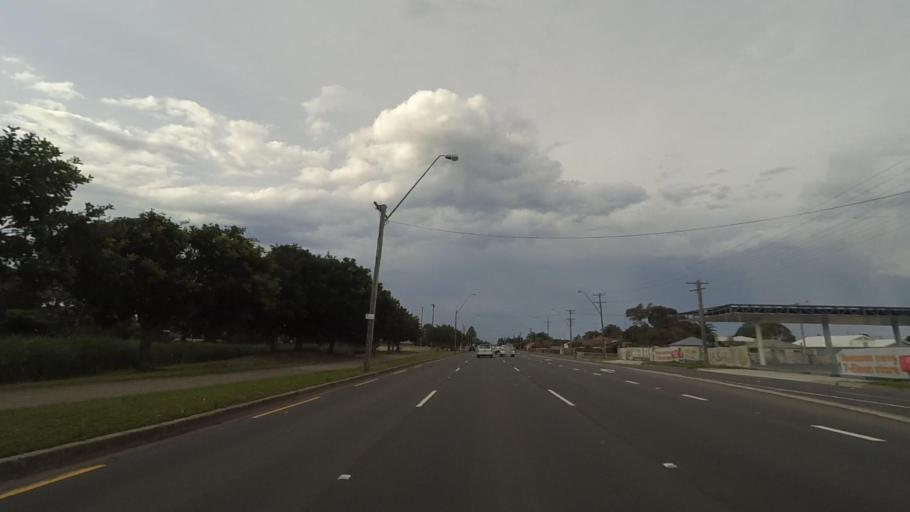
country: AU
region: New South Wales
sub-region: Shellharbour
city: Lake Illawarra
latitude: -34.5446
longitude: 150.8626
